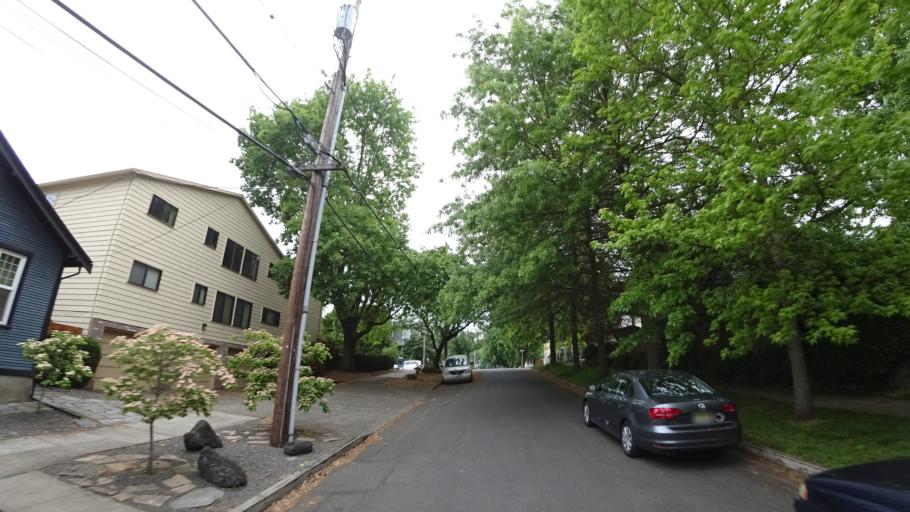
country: US
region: Oregon
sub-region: Multnomah County
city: Portland
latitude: 45.5146
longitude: -122.6425
